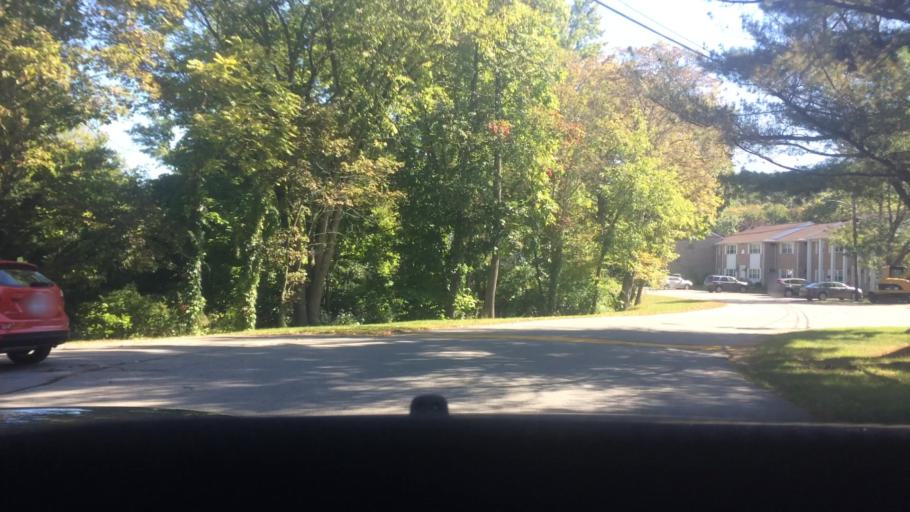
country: US
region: Massachusetts
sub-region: Essex County
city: Andover
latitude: 42.6669
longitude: -71.1469
